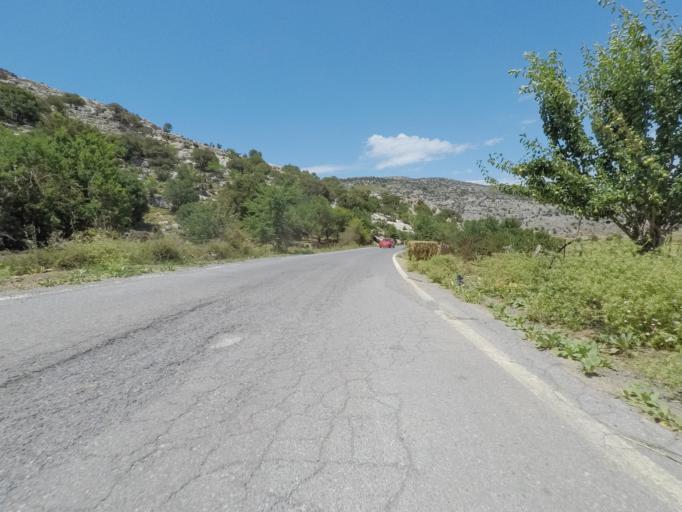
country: GR
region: Crete
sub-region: Nomos Irakleiou
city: Mokhos
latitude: 35.1881
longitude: 25.4311
